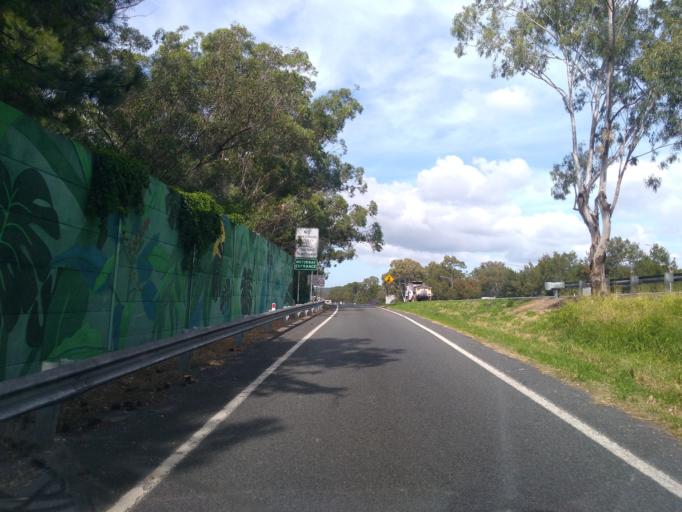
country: AU
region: Queensland
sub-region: Gold Coast
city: Palm Beach
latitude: -28.1255
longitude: 153.4653
